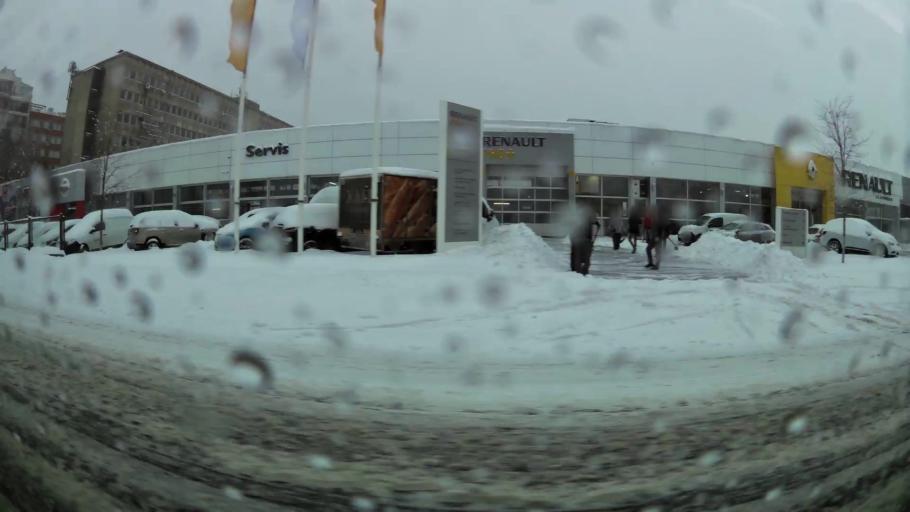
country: RS
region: Central Serbia
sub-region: Belgrade
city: Stari Grad
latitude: 44.8229
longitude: 20.4693
